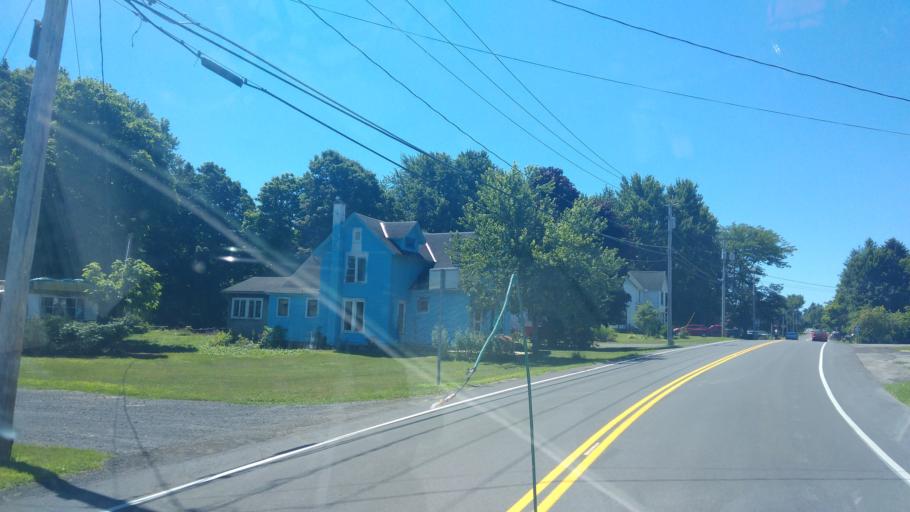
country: US
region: New York
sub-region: Wayne County
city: Sodus
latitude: 43.2109
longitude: -76.9804
